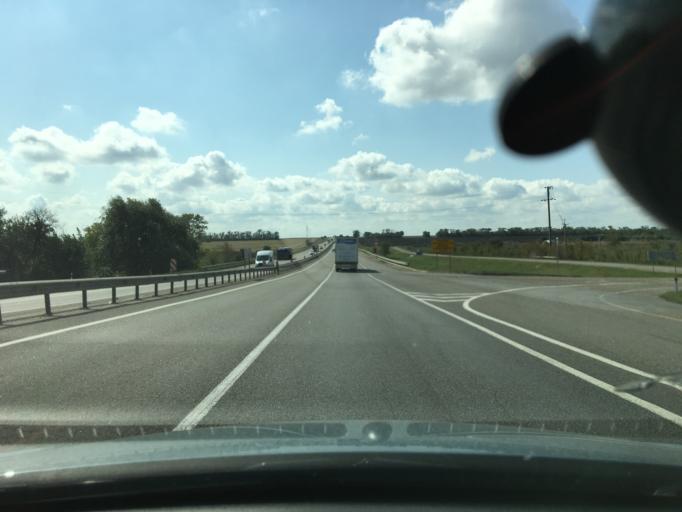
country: RU
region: Krasnodarskiy
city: Krasnoye
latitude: 46.7344
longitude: 39.6566
